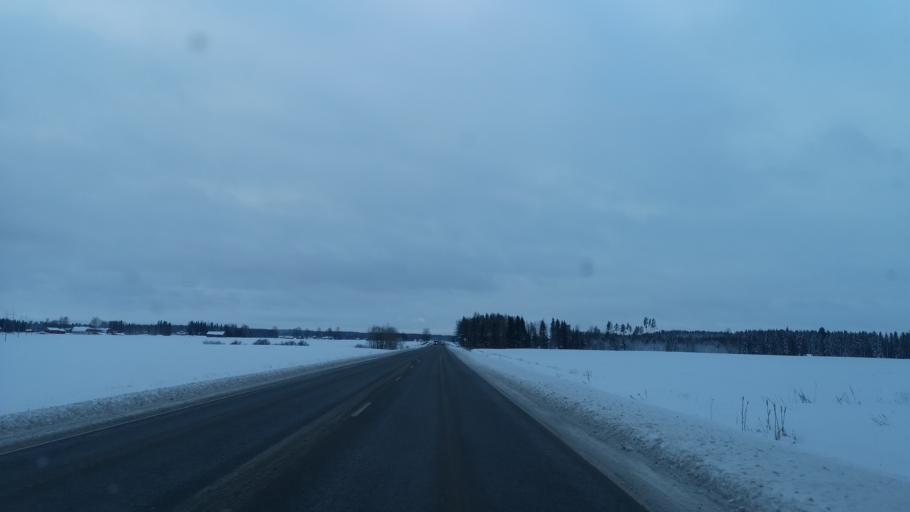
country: FI
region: Varsinais-Suomi
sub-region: Loimaa
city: Loimaa
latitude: 60.8955
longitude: 23.1206
